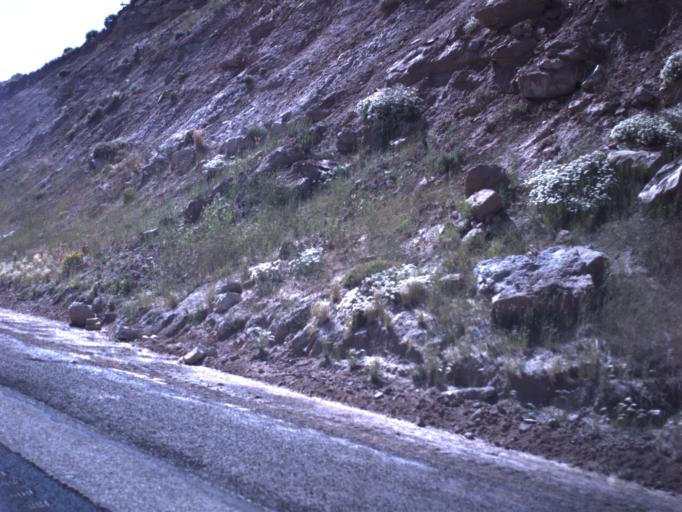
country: US
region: Utah
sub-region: Summit County
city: Francis
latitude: 40.1855
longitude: -111.0235
